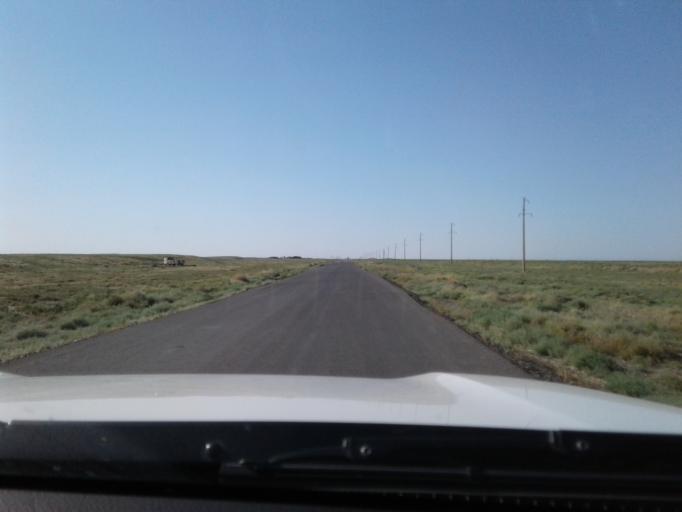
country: IR
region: Razavi Khorasan
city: Kalat-e Naderi
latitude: 37.1605
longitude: 60.0503
